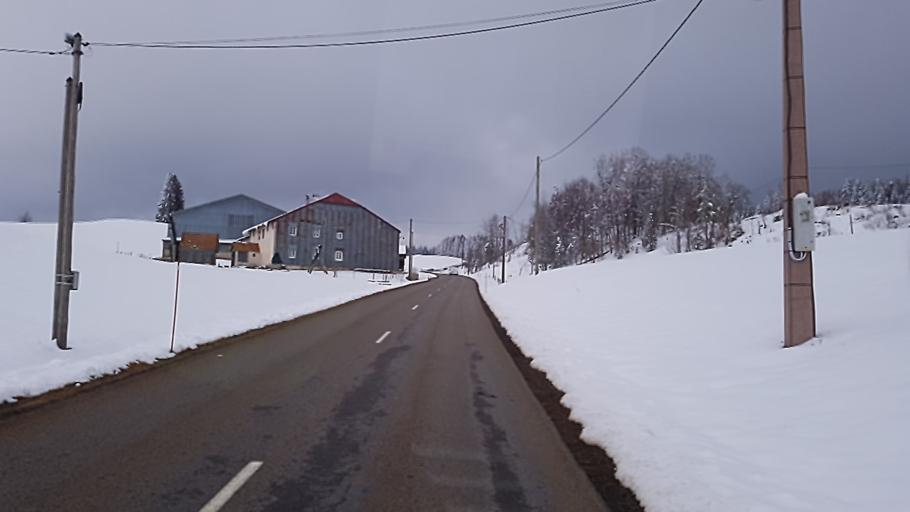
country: FR
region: Franche-Comte
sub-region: Departement du Jura
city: Longchaumois
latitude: 46.3947
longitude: 5.9522
